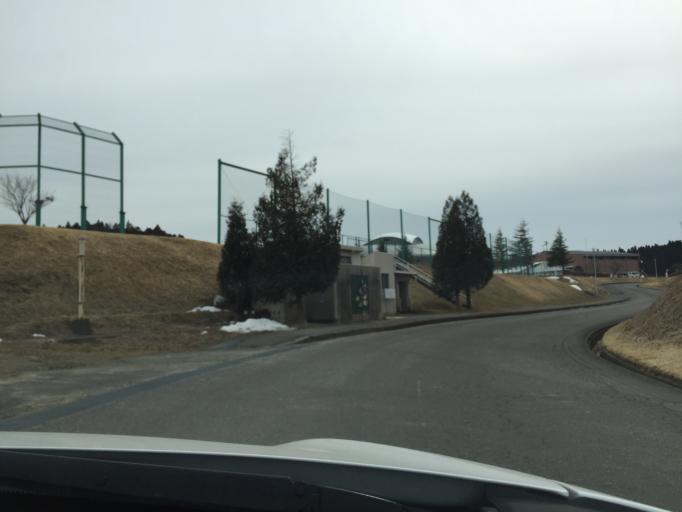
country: JP
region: Fukushima
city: Funehikimachi-funehiki
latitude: 37.2915
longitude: 140.6219
